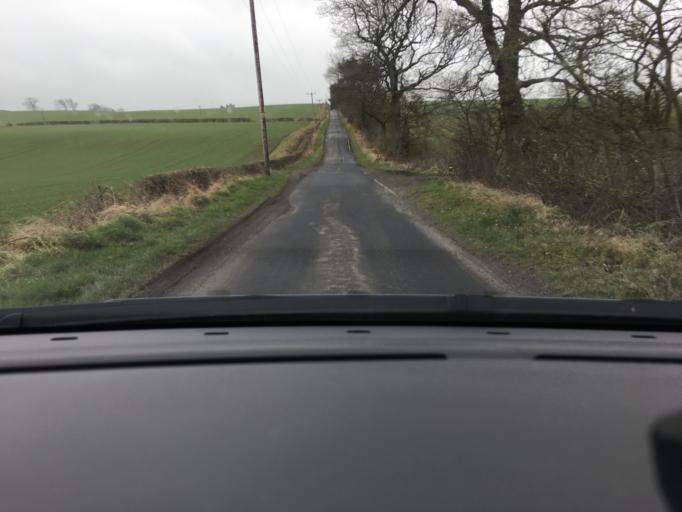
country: GB
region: Scotland
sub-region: West Lothian
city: Linlithgow
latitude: 55.9637
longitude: -3.5549
